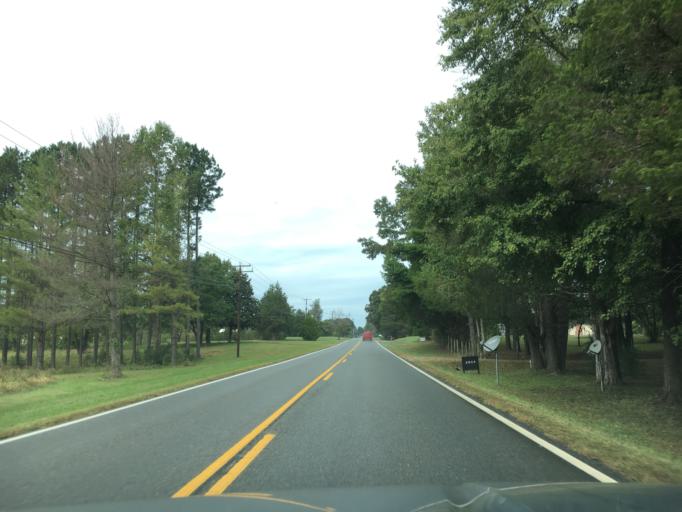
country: US
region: Virginia
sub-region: Goochland County
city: Goochland
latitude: 37.7244
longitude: -77.8303
